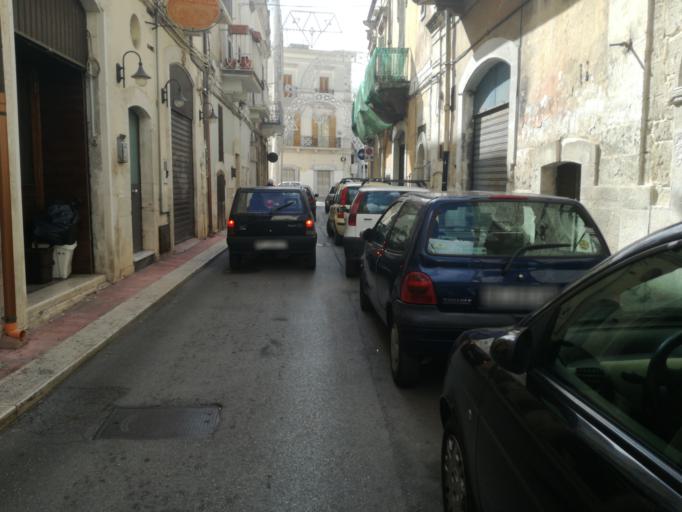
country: IT
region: Apulia
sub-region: Provincia di Bari
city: Triggiano
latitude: 41.0645
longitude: 16.9227
